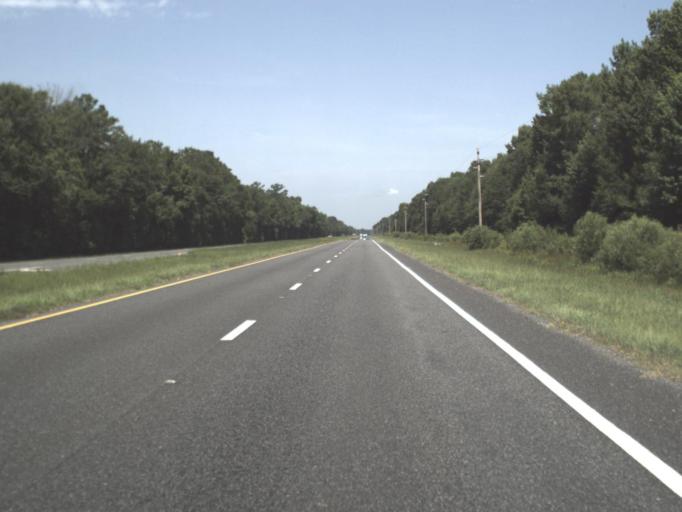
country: US
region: Florida
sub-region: Dixie County
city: Cross City
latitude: 29.6692
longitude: -83.2237
